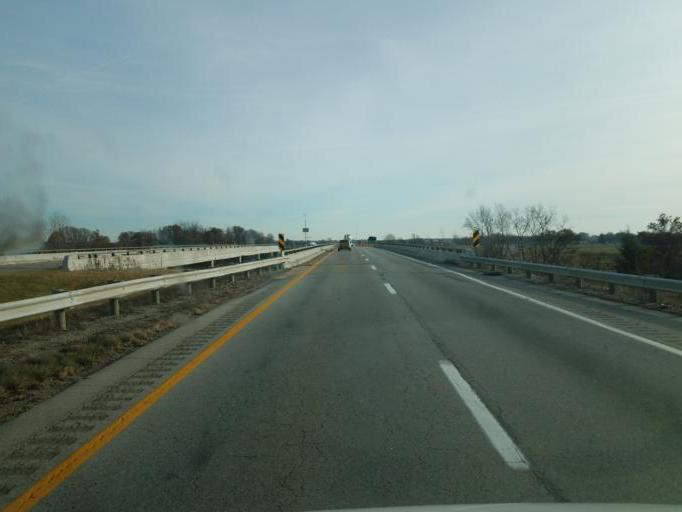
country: US
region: Ohio
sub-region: Marion County
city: Marion
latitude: 40.6013
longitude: -83.0874
